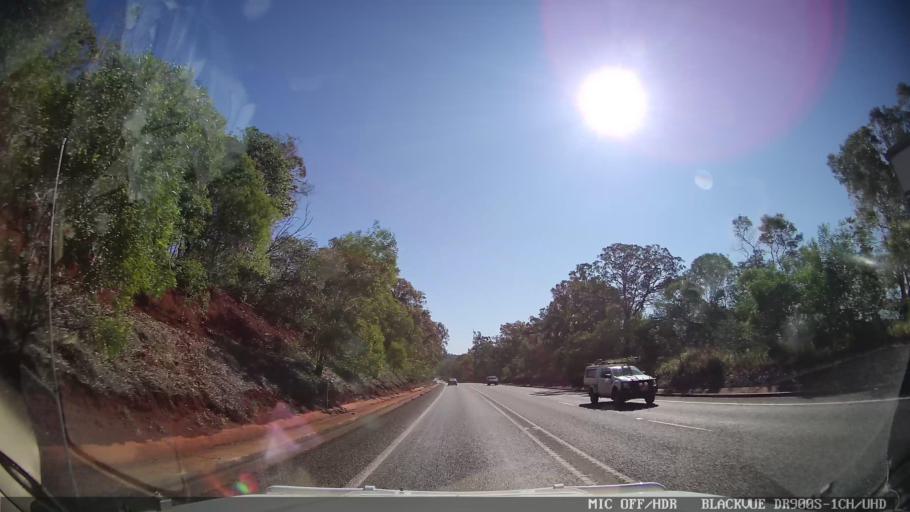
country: AU
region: Queensland
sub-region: Bundaberg
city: Childers
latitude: -25.2349
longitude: 152.2498
